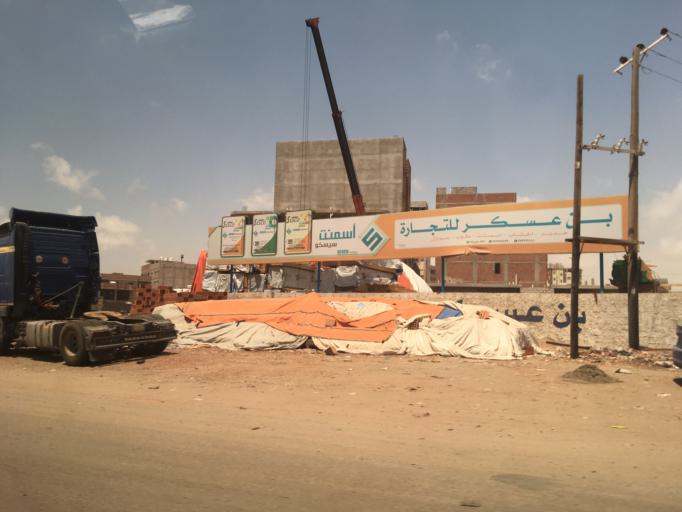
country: YE
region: Aden
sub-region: Al Mansura
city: Al Mansurah
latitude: 12.8690
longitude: 44.9708
